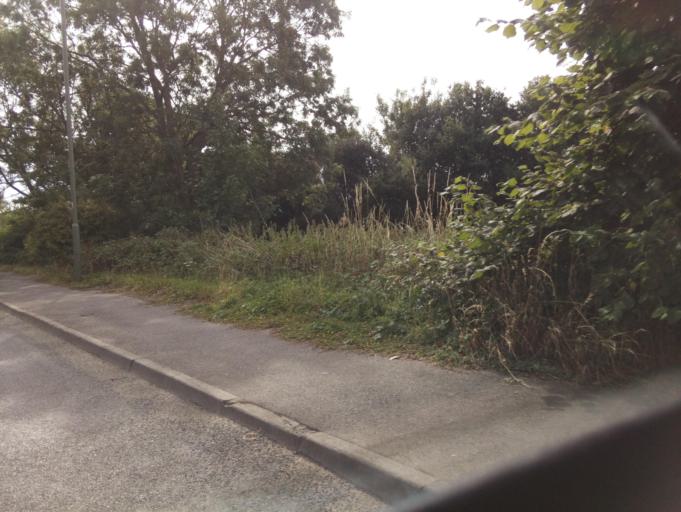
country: GB
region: England
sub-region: Surrey
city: Horley
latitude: 51.1739
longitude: -0.1451
